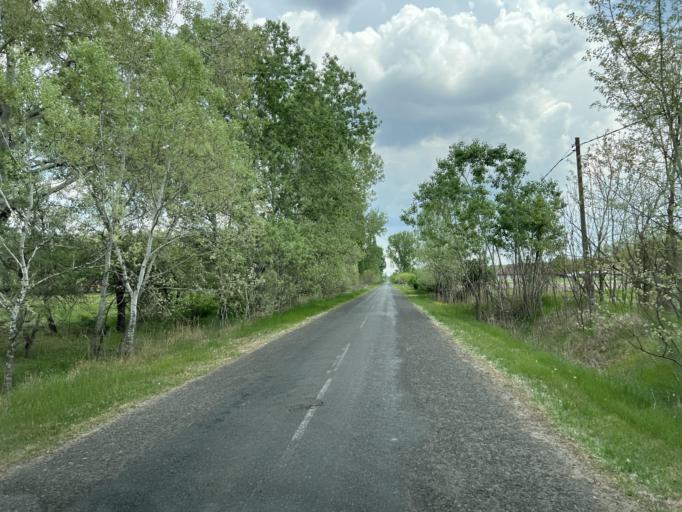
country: HU
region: Pest
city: Csemo
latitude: 47.0950
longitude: 19.7528
